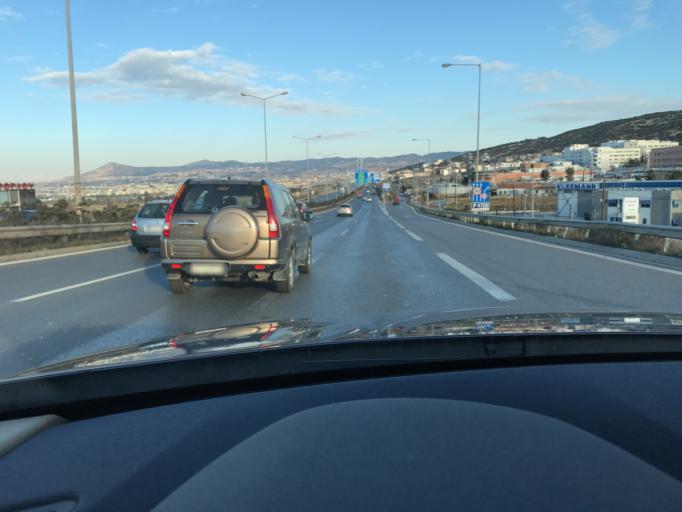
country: GR
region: Central Macedonia
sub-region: Nomos Thessalonikis
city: Polichni
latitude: 40.6695
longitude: 22.9621
